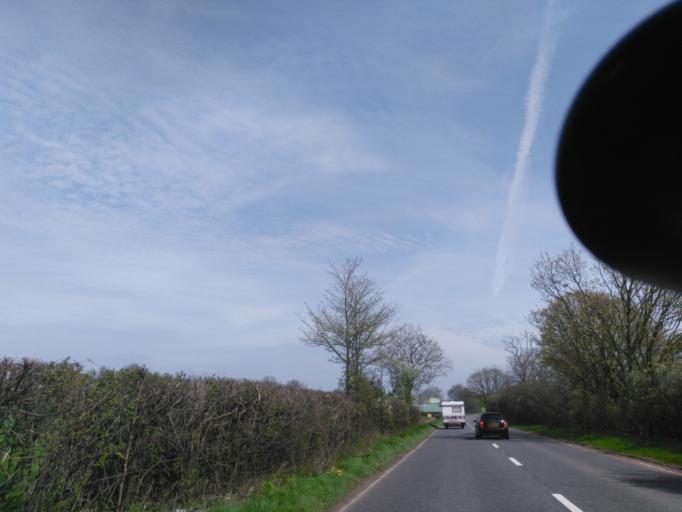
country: GB
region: England
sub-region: Somerset
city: Shepton Mallet
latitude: 51.1699
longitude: -2.5428
